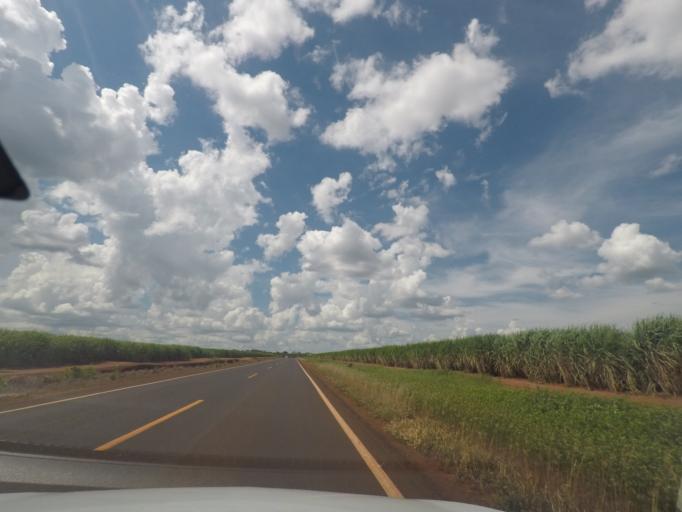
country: BR
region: Minas Gerais
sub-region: Conceicao Das Alagoas
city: Conceicao das Alagoas
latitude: -19.8562
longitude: -48.5996
